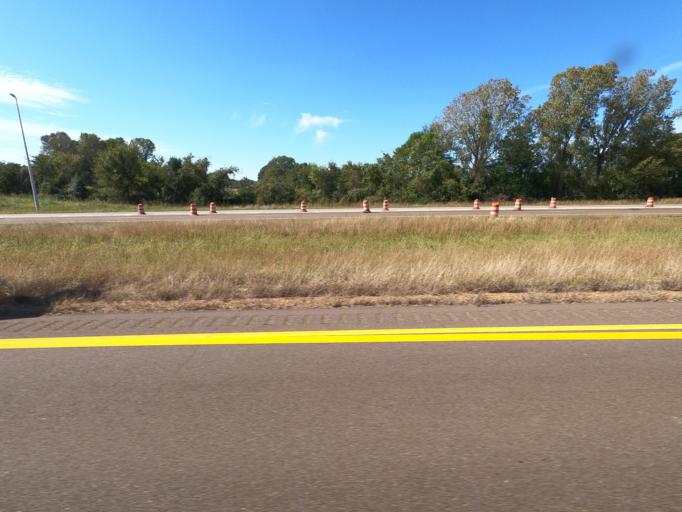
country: US
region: Tennessee
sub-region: Dyer County
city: Dyersburg
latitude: 36.0216
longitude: -89.3405
